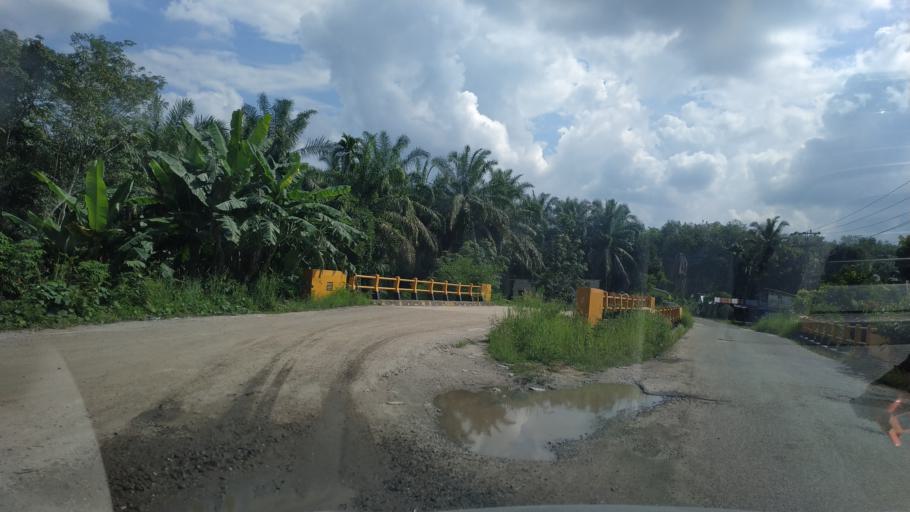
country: ID
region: North Sumatra
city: Binanga
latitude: 1.3190
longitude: 99.7549
